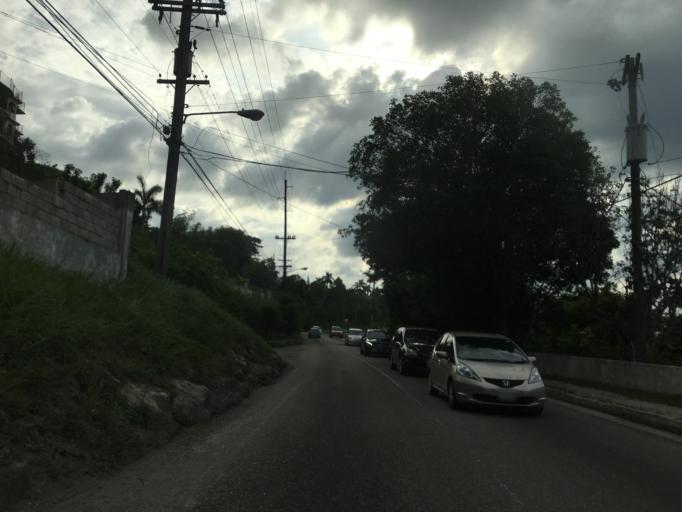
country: JM
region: Saint James
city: Montego Bay
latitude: 18.4920
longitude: -77.9198
